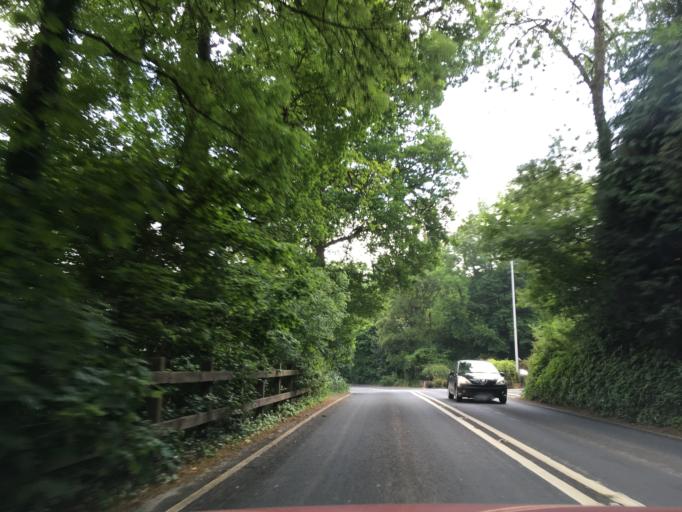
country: GB
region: England
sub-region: Devon
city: Totnes
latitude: 50.4435
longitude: -3.7025
